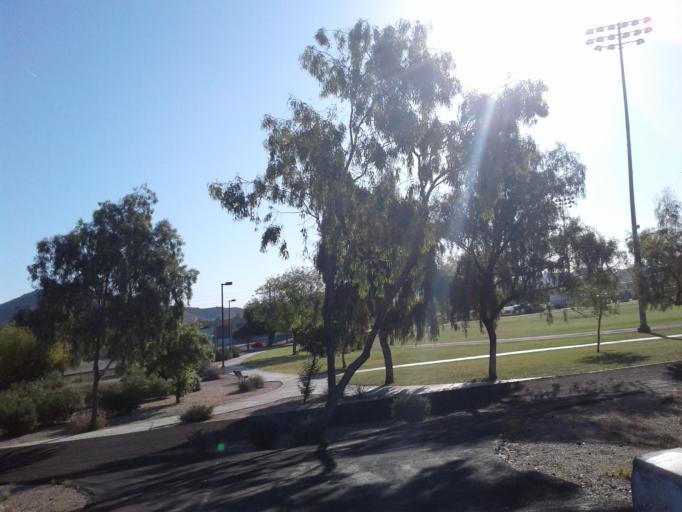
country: US
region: Arizona
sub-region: Maricopa County
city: Glendale
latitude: 33.5780
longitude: -112.1102
